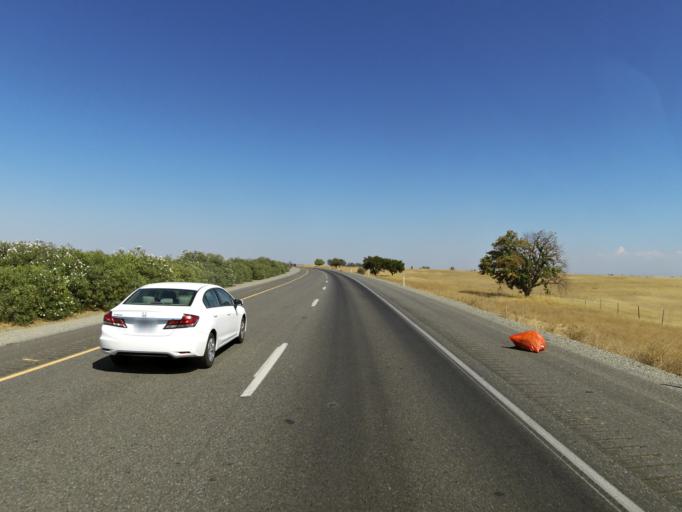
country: US
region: California
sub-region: Glenn County
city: Orland
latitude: 39.8007
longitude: -122.1999
